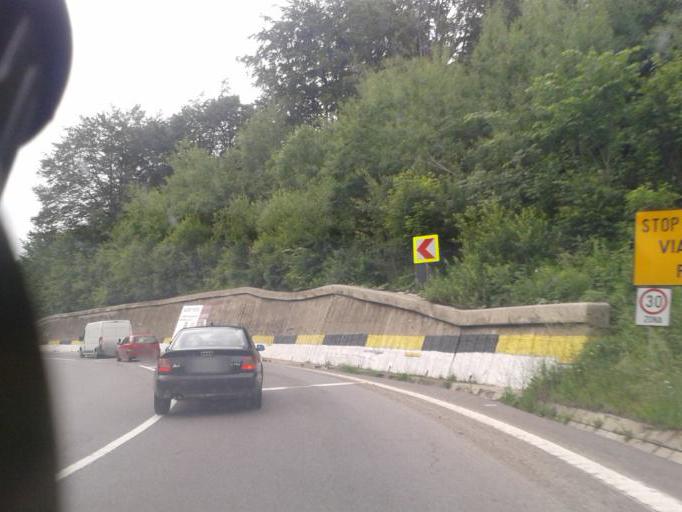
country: RO
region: Brasov
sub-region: Oras Predeal
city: Predeal
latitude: 45.5165
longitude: 25.5782
